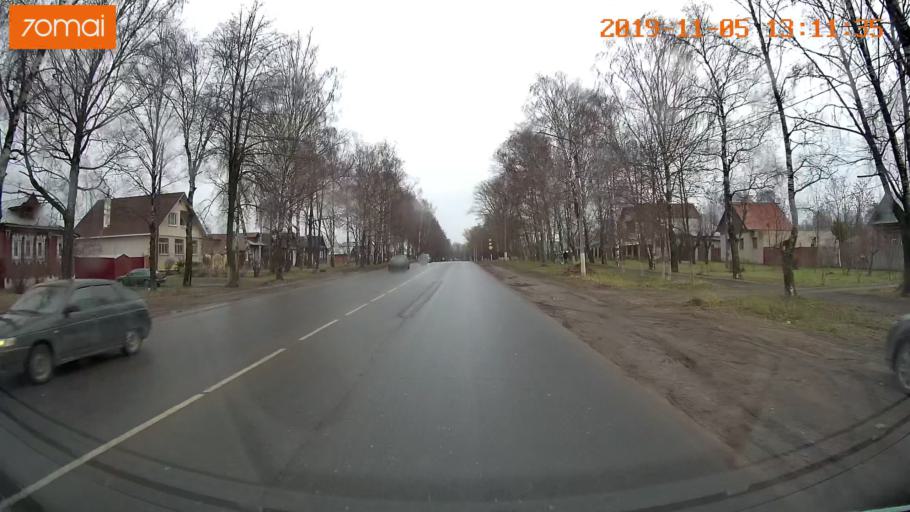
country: RU
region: Ivanovo
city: Shuya
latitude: 56.8586
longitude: 41.3412
